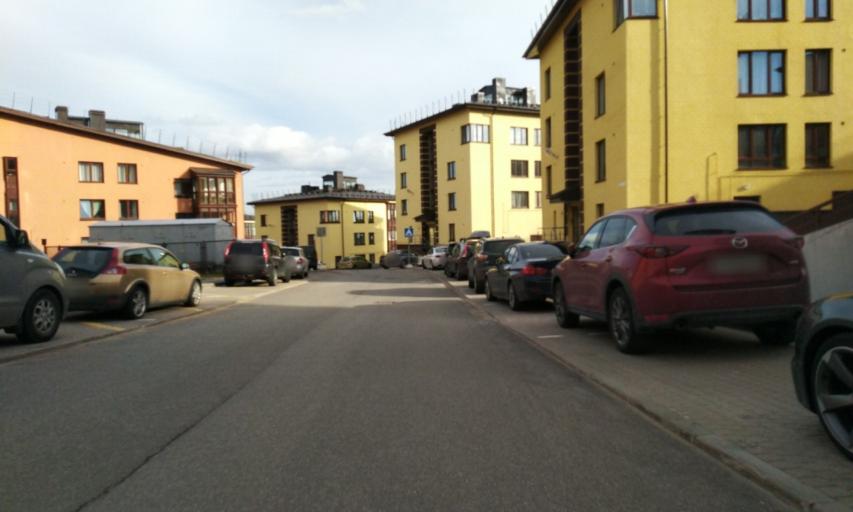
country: RU
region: Leningrad
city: Bugry
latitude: 60.1194
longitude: 30.4238
